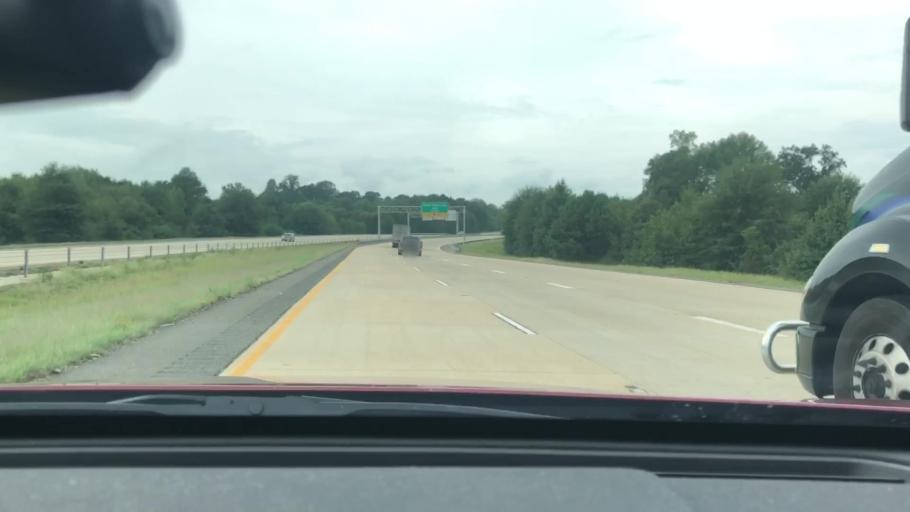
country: US
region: Texas
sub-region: Bowie County
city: Texarkana
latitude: 33.3855
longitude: -94.0296
